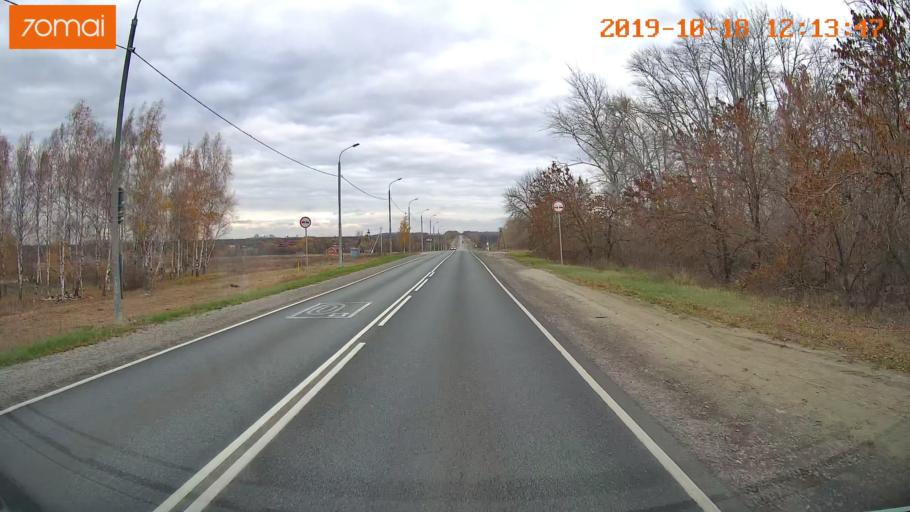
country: RU
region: Rjazan
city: Zakharovo
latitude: 54.4234
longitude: 39.3733
